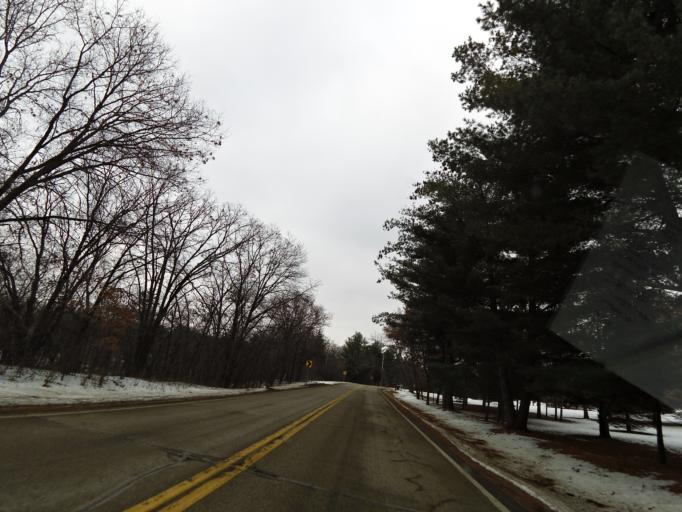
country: US
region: Minnesota
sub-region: Washington County
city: Afton
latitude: 44.9125
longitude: -92.7865
